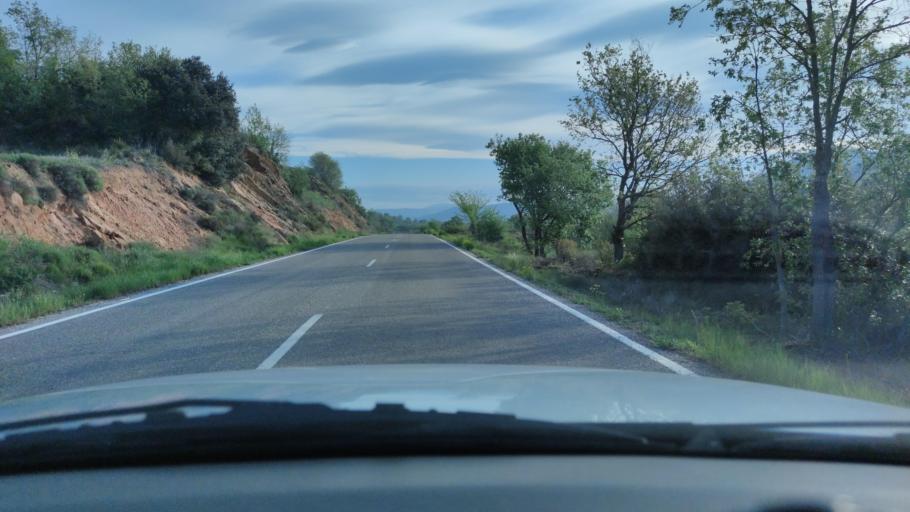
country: ES
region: Catalonia
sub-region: Provincia de Lleida
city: Ponts
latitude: 41.8835
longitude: 1.1814
